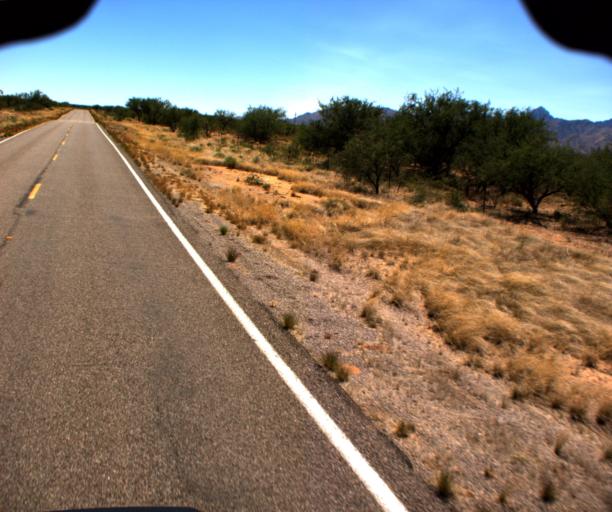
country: US
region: Arizona
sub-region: Pima County
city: Three Points
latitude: 31.8153
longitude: -111.4413
